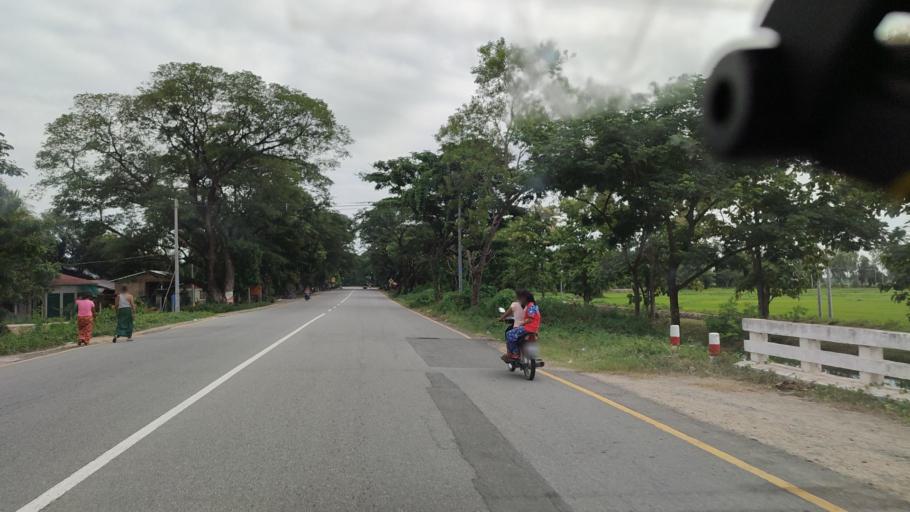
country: MM
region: Mandalay
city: Pyinmana
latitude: 19.8416
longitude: 96.2602
